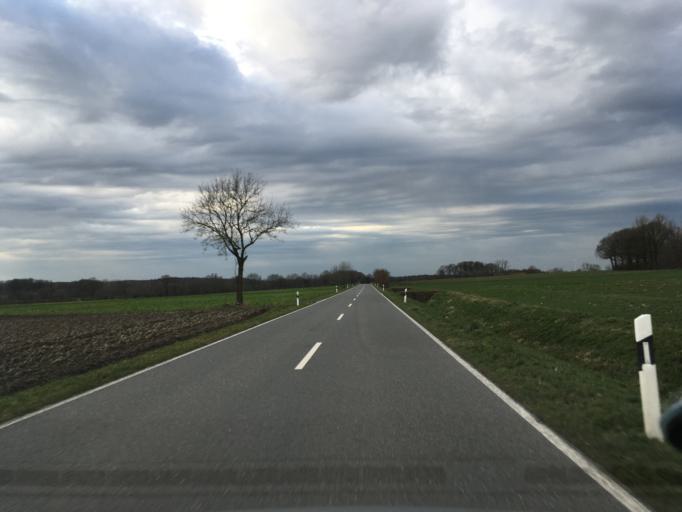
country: DE
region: North Rhine-Westphalia
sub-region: Regierungsbezirk Munster
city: Schoppingen
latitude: 52.0552
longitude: 7.1739
